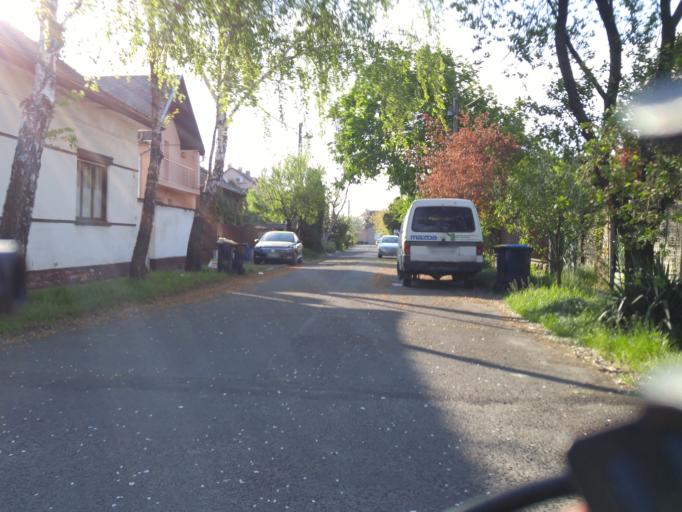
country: HU
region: Budapest
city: Budapest XIX. keruelet
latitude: 47.4358
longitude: 19.1292
